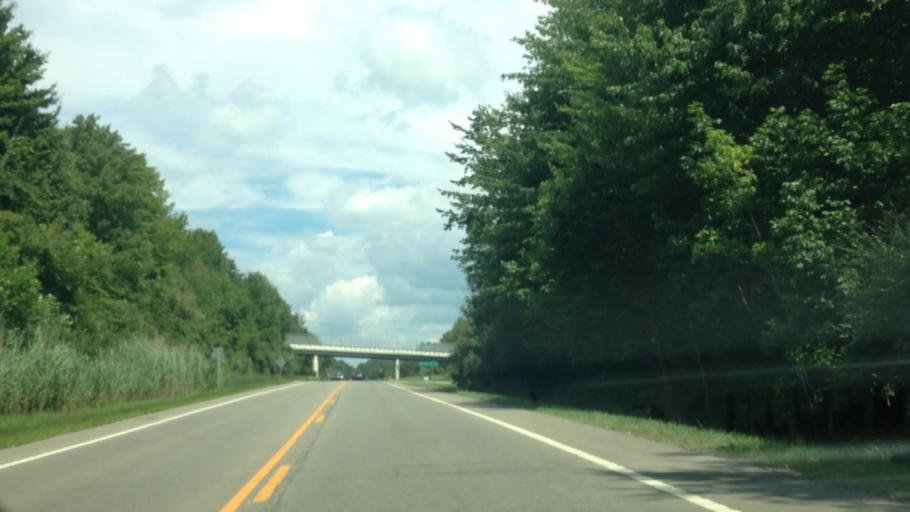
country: US
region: Ohio
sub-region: Wayne County
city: Doylestown
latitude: 40.9673
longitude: -81.7108
